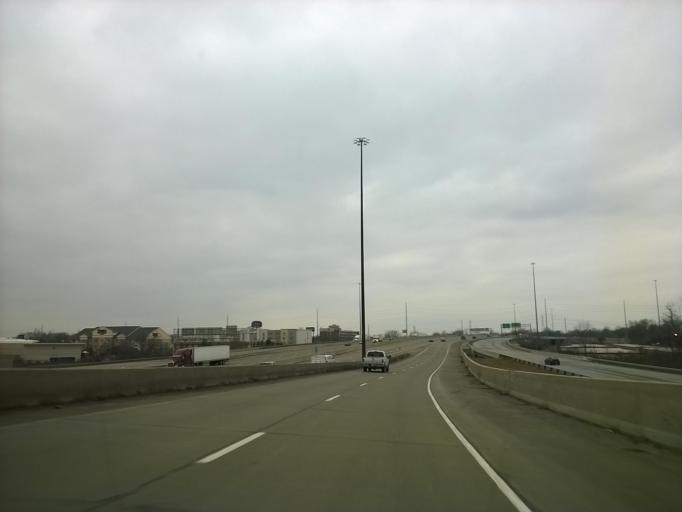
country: US
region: Indiana
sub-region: Marion County
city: Warren Park
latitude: 39.7990
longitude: -86.0401
